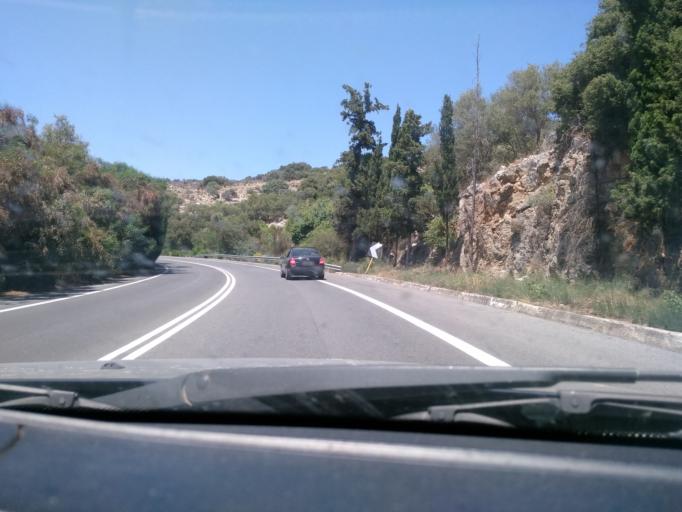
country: GR
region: Crete
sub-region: Nomos Chanias
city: Kalivai
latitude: 35.4262
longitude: 24.1704
